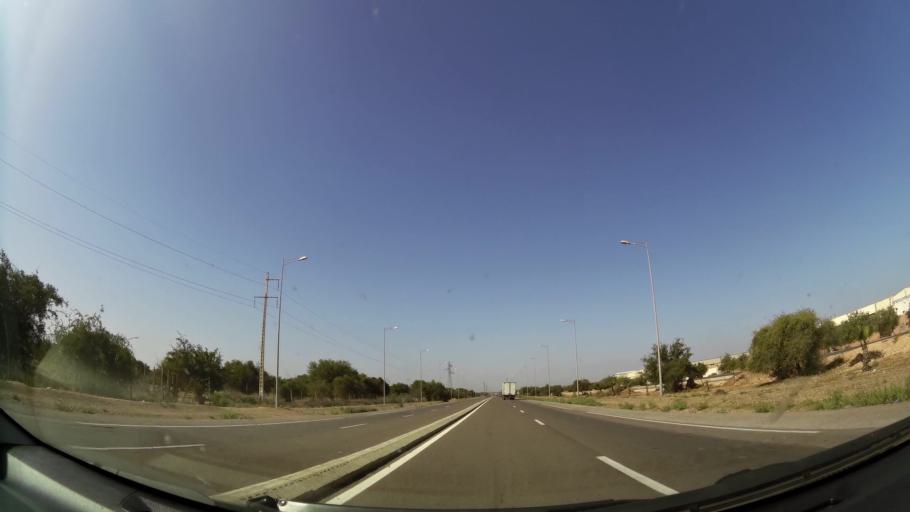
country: MA
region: Souss-Massa-Draa
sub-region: Inezgane-Ait Mellou
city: Inezgane
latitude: 30.3199
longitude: -9.4896
